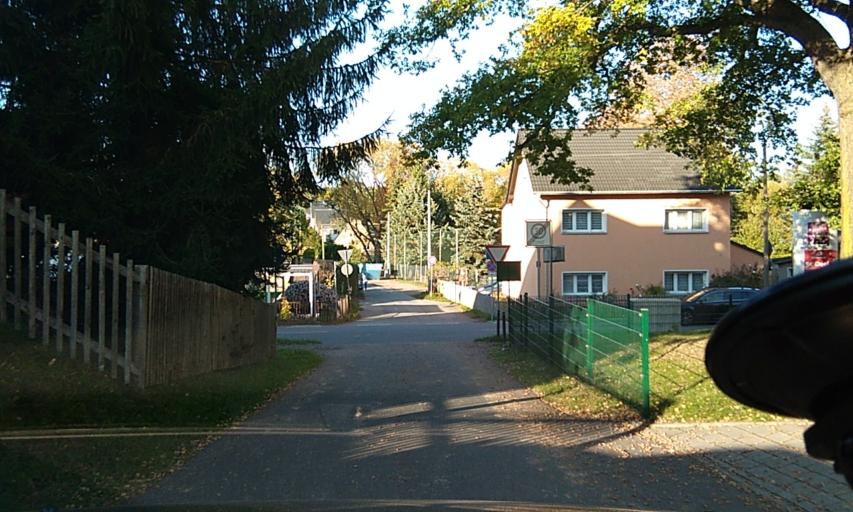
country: DE
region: Saxony
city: Wittgensdorf
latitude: 50.8356
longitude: 12.8563
